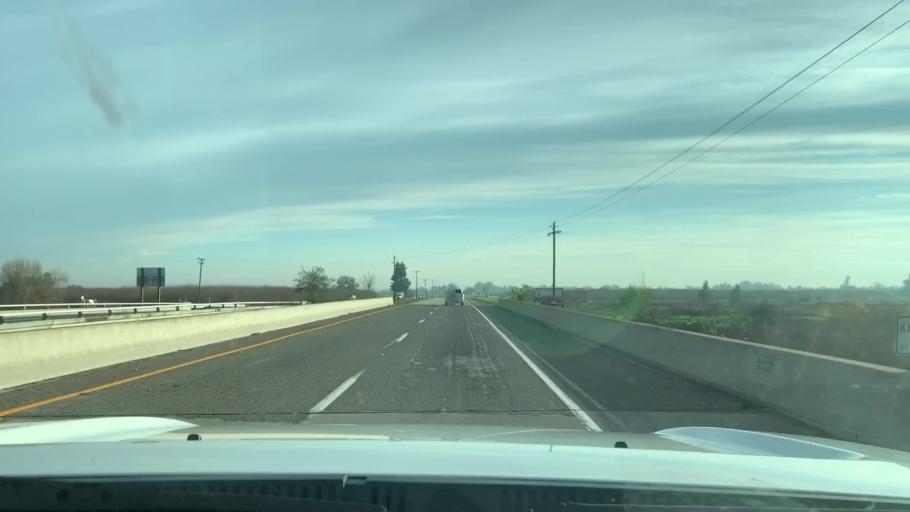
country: US
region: California
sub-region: Fresno County
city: Riverdale
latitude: 36.3865
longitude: -119.8098
